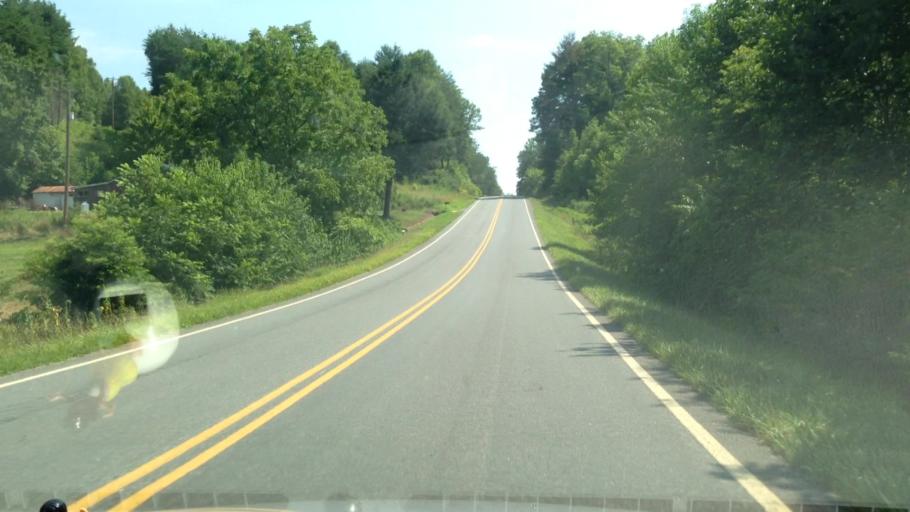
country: US
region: North Carolina
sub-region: Surry County
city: Flat Rock
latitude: 36.5709
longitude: -80.4546
